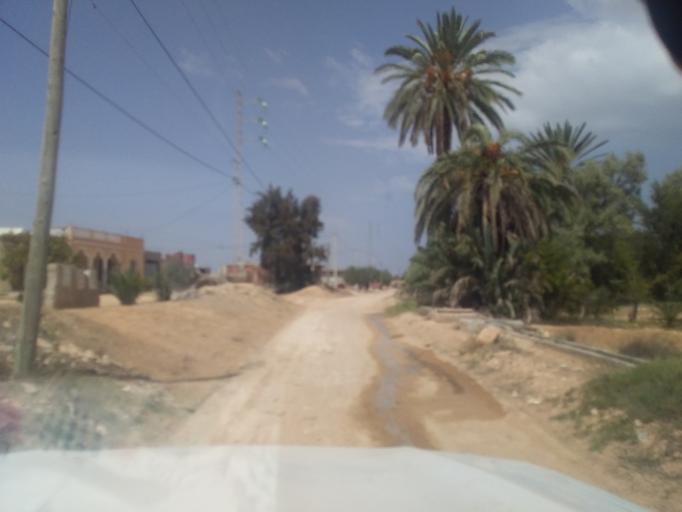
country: TN
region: Madanin
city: Medenine
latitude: 33.5931
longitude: 10.3261
